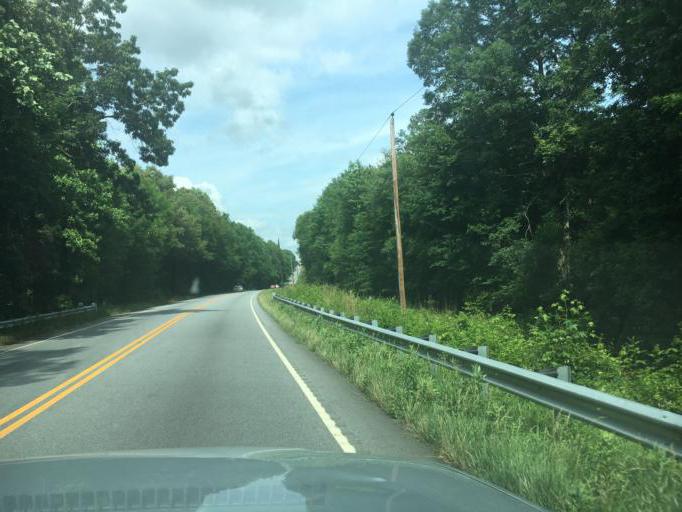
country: US
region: South Carolina
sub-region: Greenville County
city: Simpsonville
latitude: 34.6592
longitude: -82.2764
